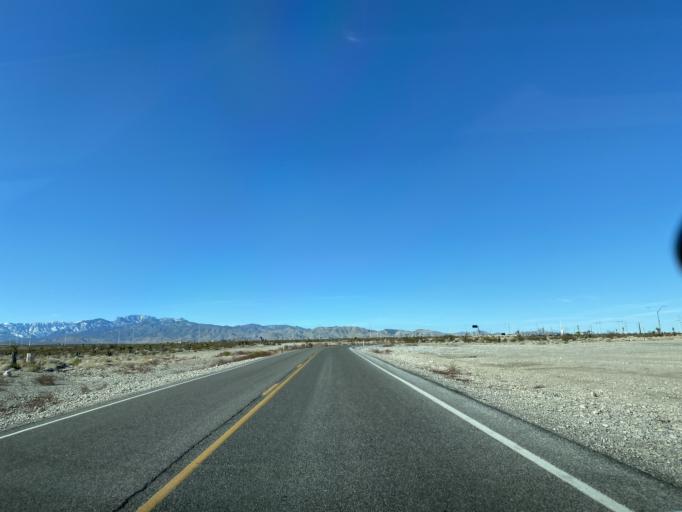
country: US
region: Nevada
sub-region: Clark County
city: Summerlin South
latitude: 36.3248
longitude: -115.3145
